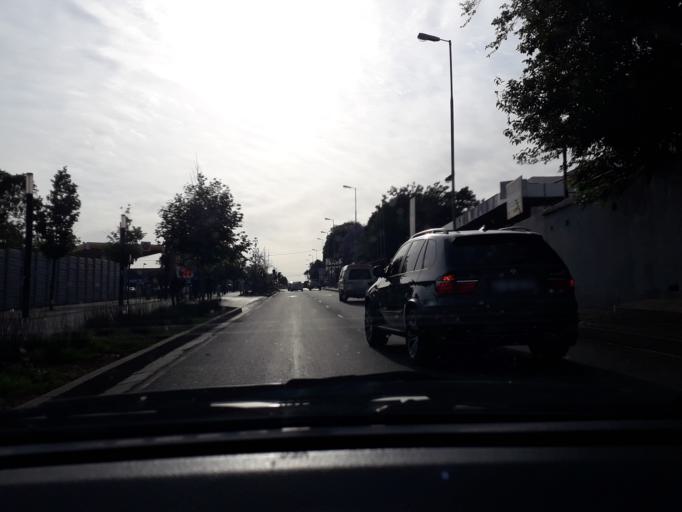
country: ZA
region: Gauteng
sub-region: City of Johannesburg Metropolitan Municipality
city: Modderfontein
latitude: -26.1097
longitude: 28.0782
